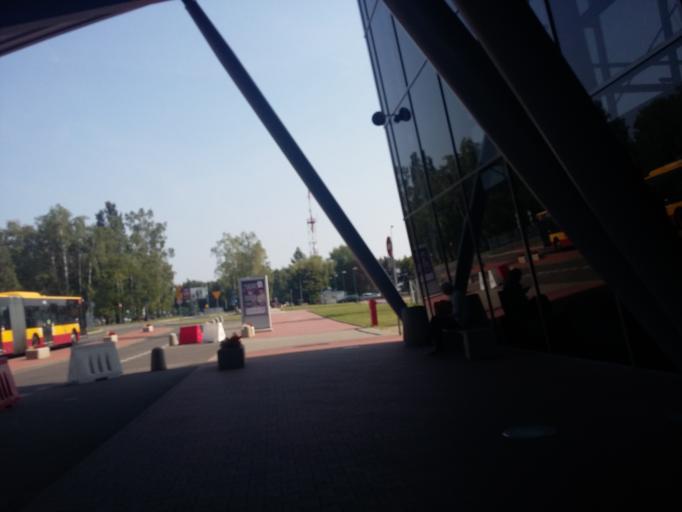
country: PL
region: Lodz Voivodeship
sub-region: Powiat pabianicki
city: Ksawerow
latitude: 51.7275
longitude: 19.4016
